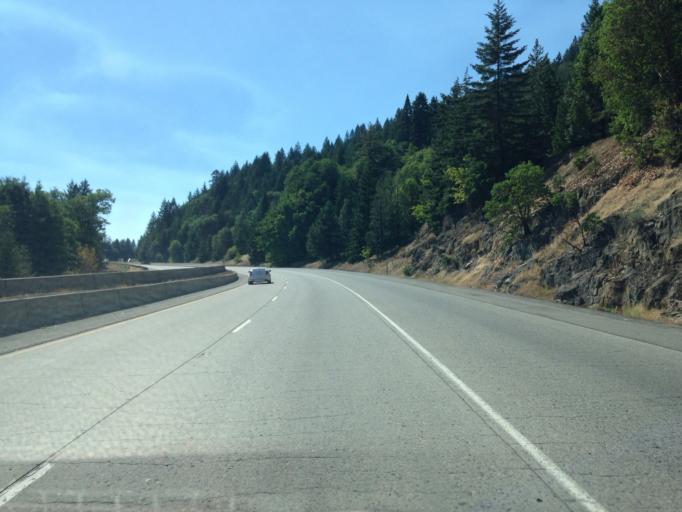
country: US
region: Oregon
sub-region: Jackson County
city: Ashland
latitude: 42.1069
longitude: -122.6124
